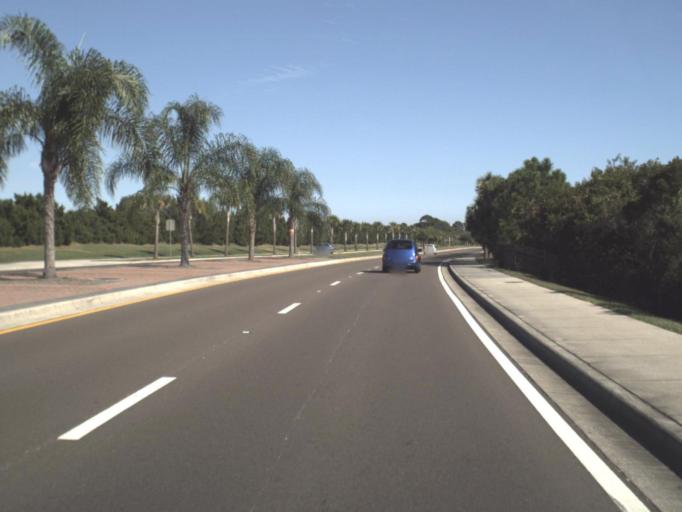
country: US
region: Florida
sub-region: Brevard County
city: South Patrick Shores
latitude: 28.2004
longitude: -80.6821
